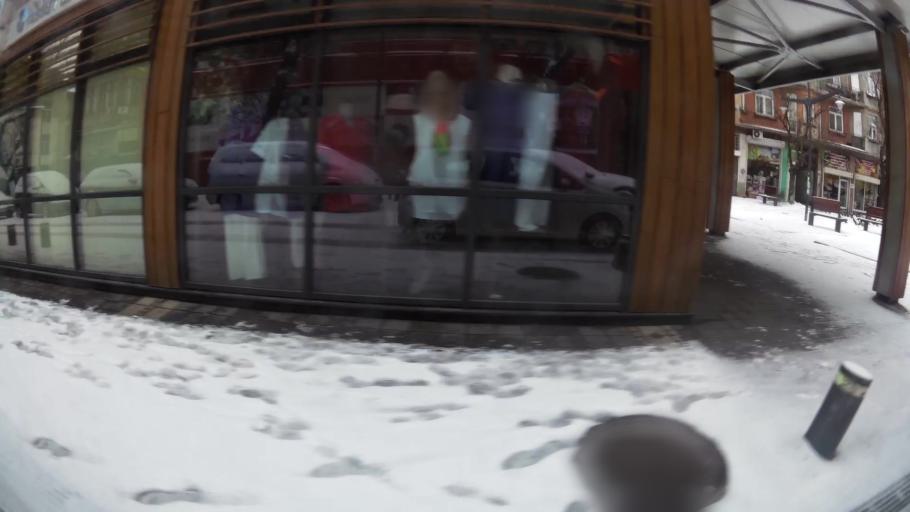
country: BG
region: Sofia-Capital
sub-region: Stolichna Obshtina
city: Sofia
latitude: 42.7024
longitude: 23.3194
